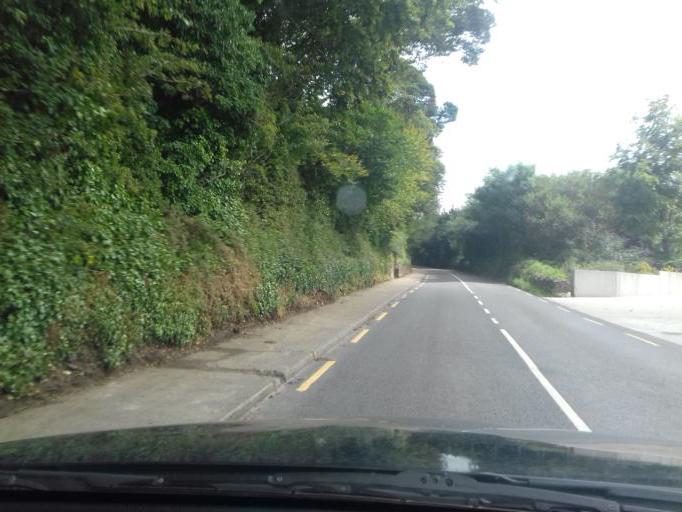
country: IE
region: Leinster
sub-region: Loch Garman
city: Enniscorthy
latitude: 52.5072
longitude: -6.5540
